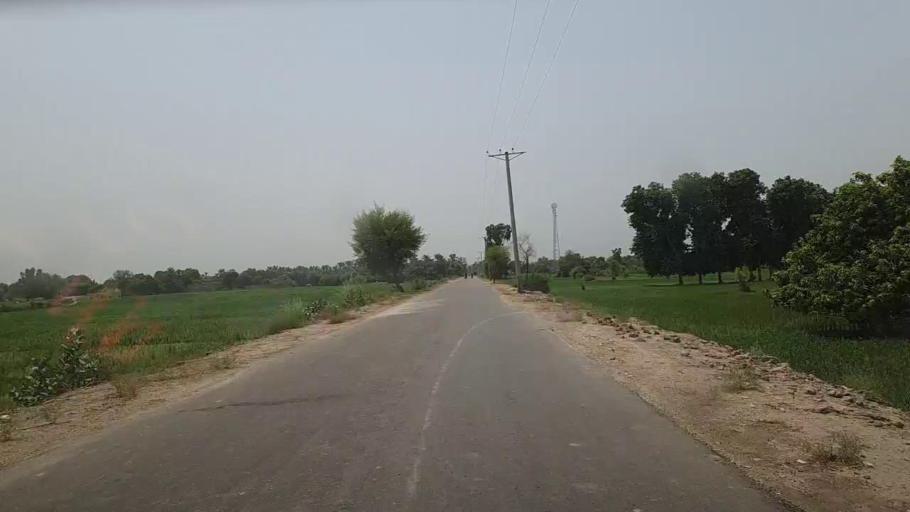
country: PK
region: Sindh
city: Sita Road
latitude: 27.0441
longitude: 67.9004
